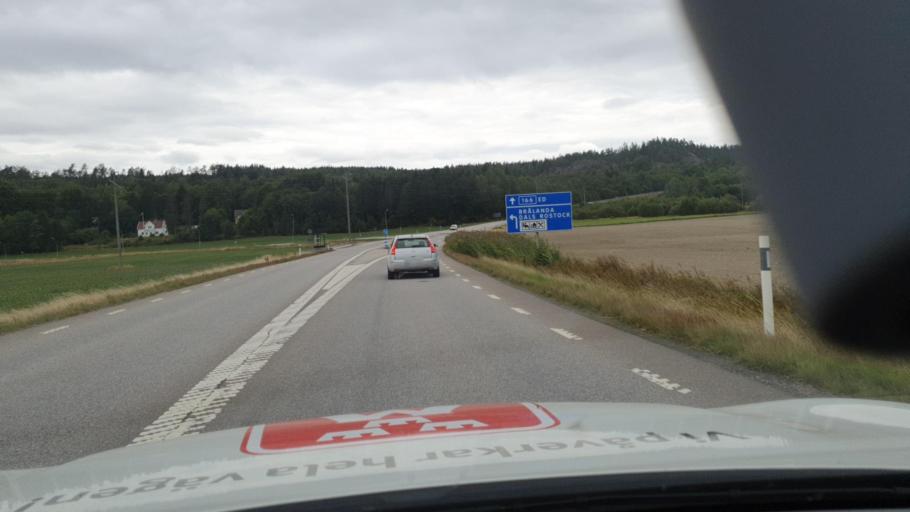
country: SE
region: Vaestra Goetaland
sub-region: Melleruds Kommun
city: Mellerud
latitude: 58.7278
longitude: 12.3688
